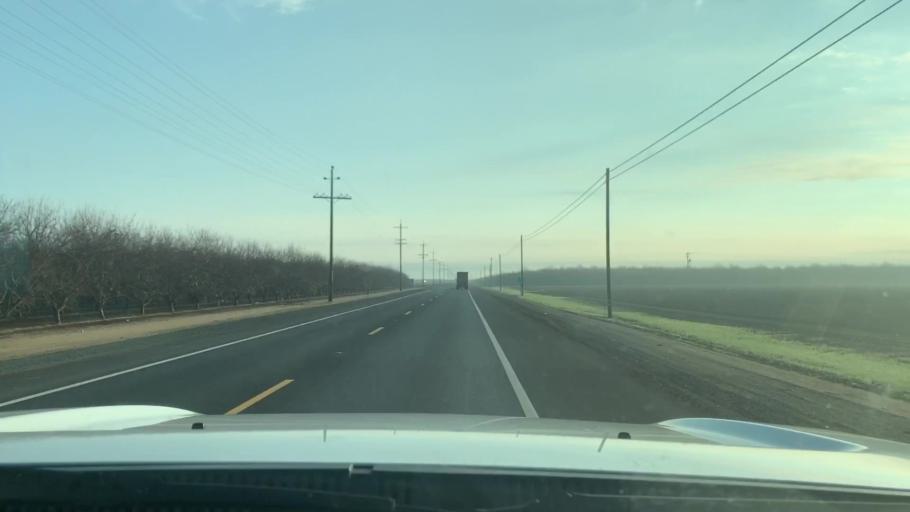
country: US
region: California
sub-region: Kern County
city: Wasco
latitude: 35.6016
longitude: -119.3156
